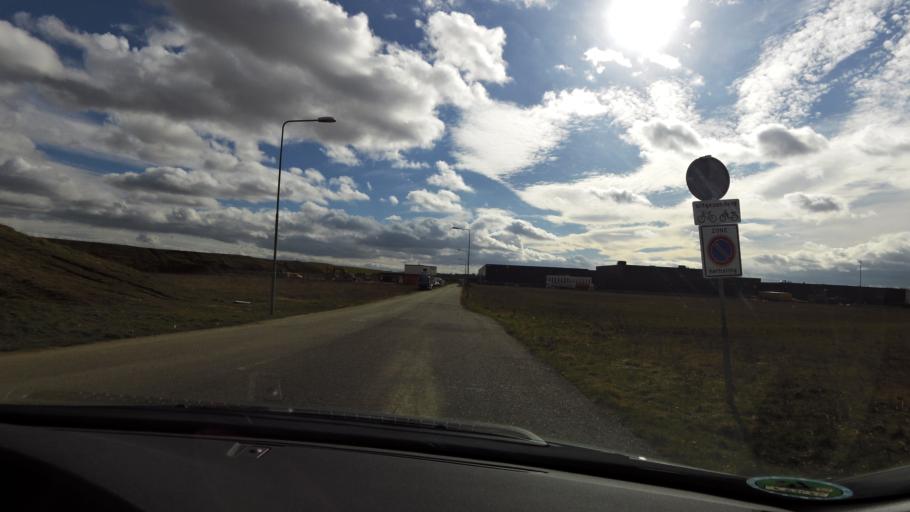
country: NL
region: Limburg
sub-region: Gemeente Beek
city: Beek
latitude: 50.9190
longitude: 5.7885
